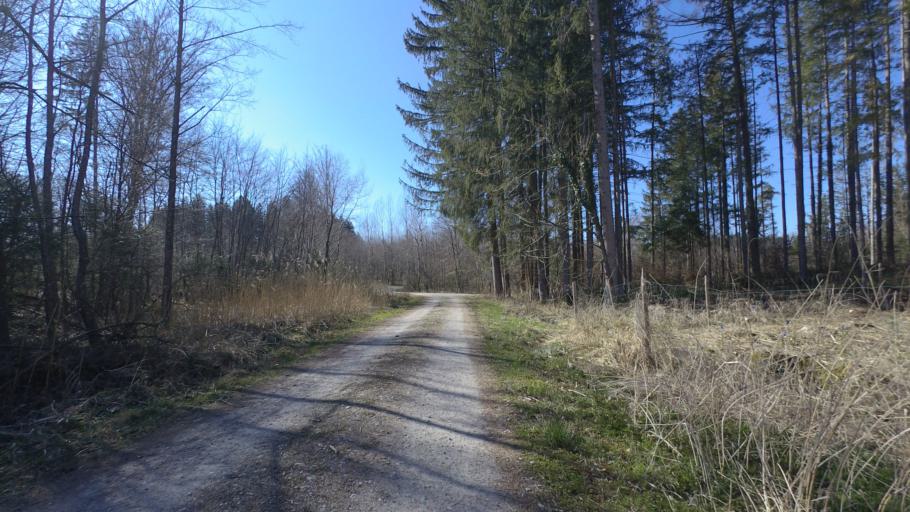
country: DE
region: Bavaria
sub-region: Upper Bavaria
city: Seeon-Seebruck
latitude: 47.9652
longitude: 12.4879
